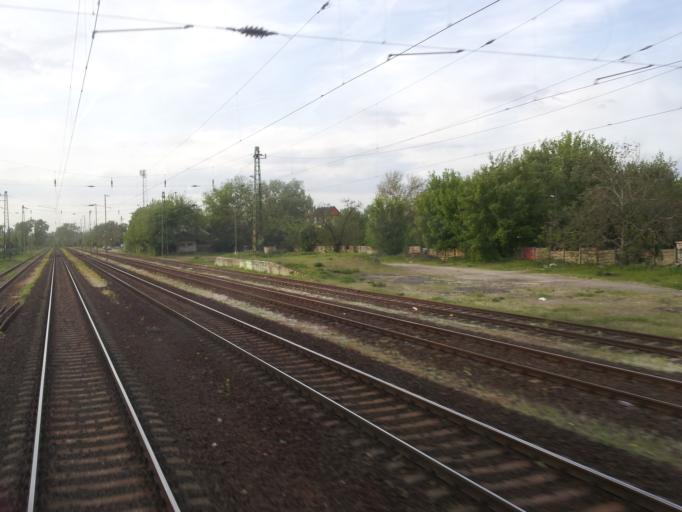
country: HU
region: Budapest
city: Budapest XVI. keruelet
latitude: 47.5201
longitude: 19.1471
